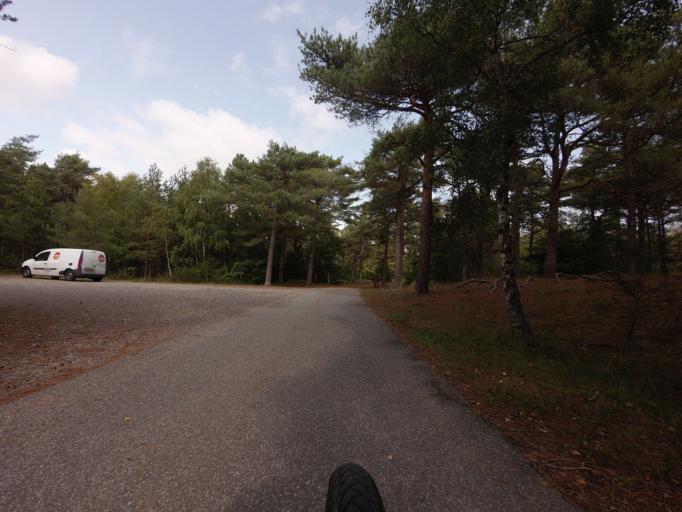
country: DK
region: North Denmark
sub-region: Frederikshavn Kommune
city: Strandby
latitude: 57.6304
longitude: 10.4354
